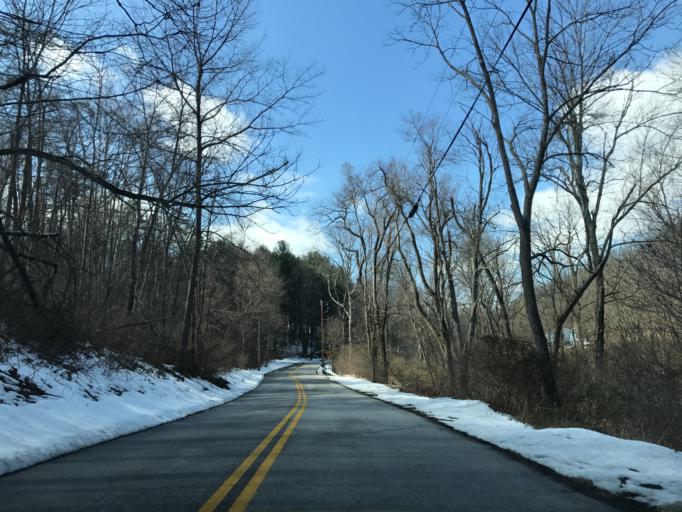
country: US
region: Maryland
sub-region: Carroll County
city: Hampstead
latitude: 39.6552
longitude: -76.8096
